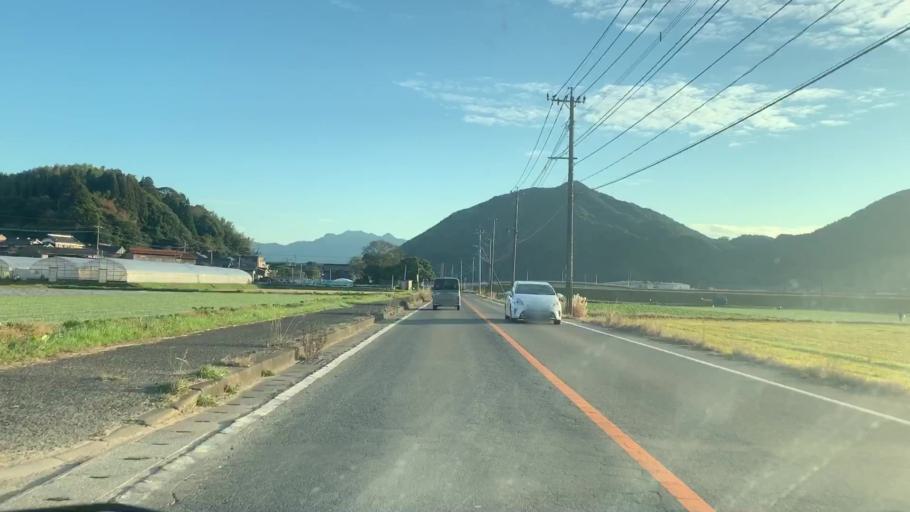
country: JP
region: Saga Prefecture
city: Karatsu
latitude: 33.3790
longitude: 129.9994
